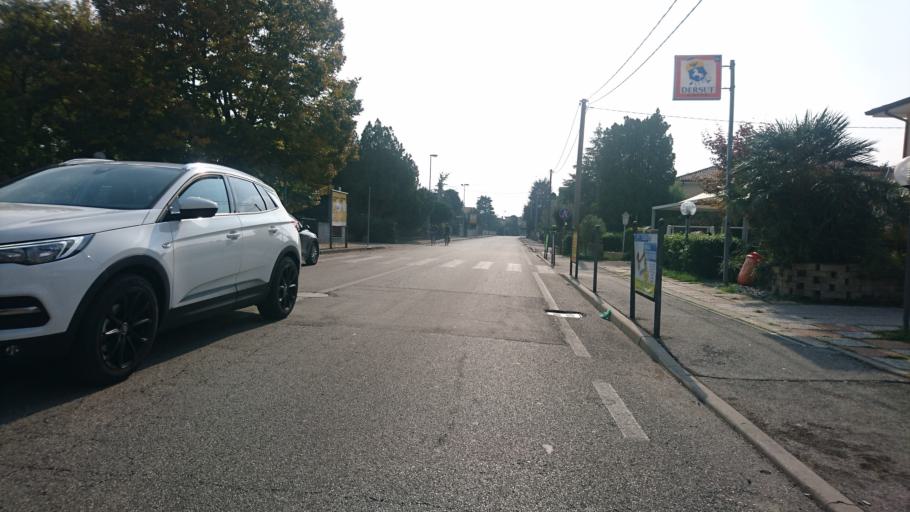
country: IT
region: Veneto
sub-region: Provincia di Rovigo
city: Rovigo
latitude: 45.0600
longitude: 11.7828
